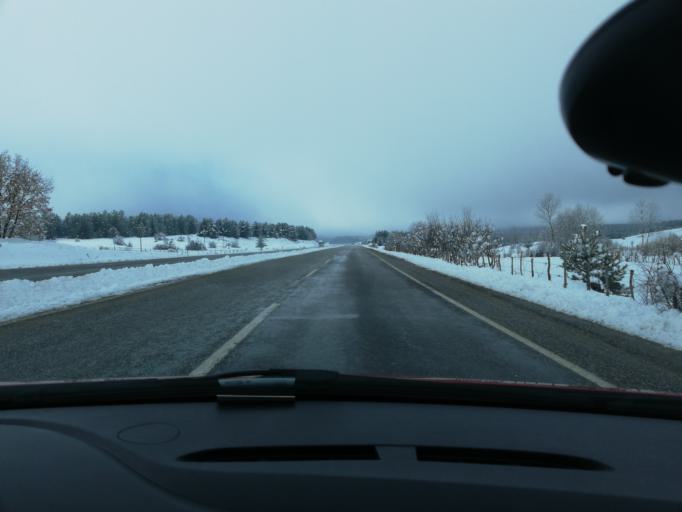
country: TR
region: Kastamonu
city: Ihsangazi
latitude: 41.3043
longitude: 33.5660
